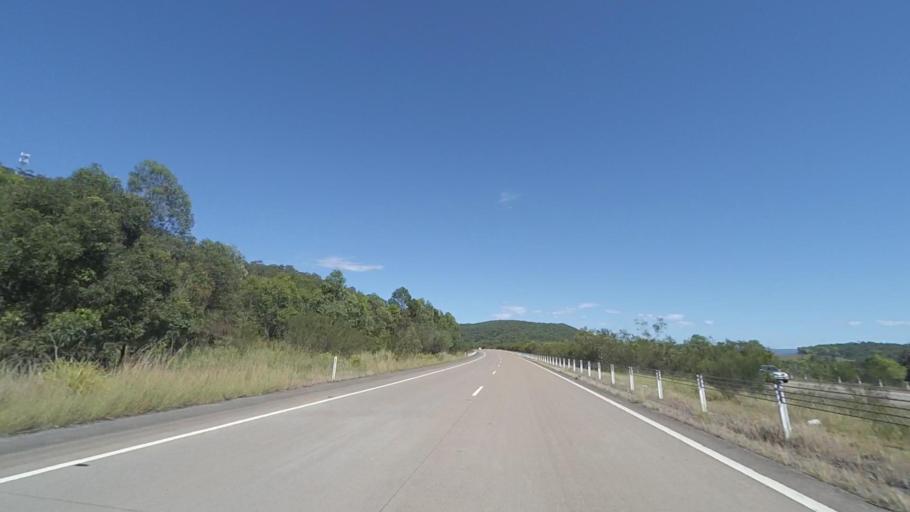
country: AU
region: New South Wales
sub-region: Port Stephens Shire
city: Port Stephens
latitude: -32.6263
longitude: 151.9879
